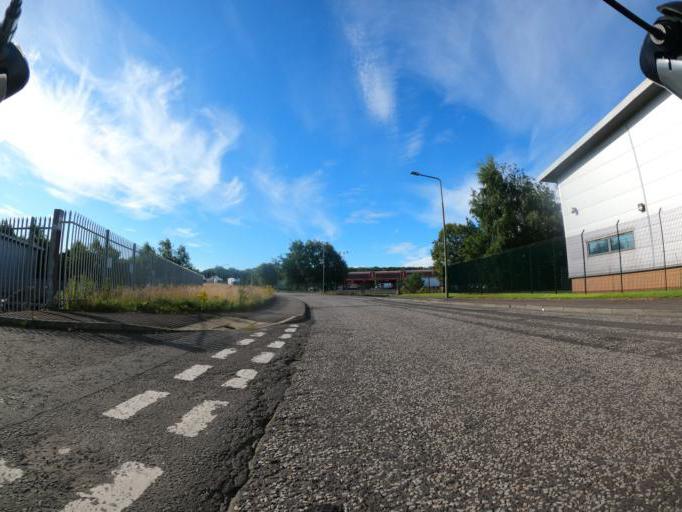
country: GB
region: Scotland
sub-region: Edinburgh
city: Newbridge
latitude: 55.9364
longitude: -3.4069
